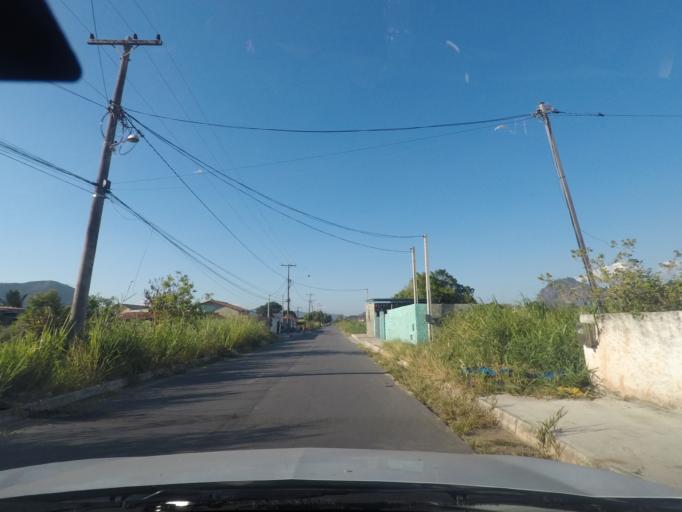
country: BR
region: Rio de Janeiro
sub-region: Marica
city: Marica
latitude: -22.9633
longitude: -42.9388
